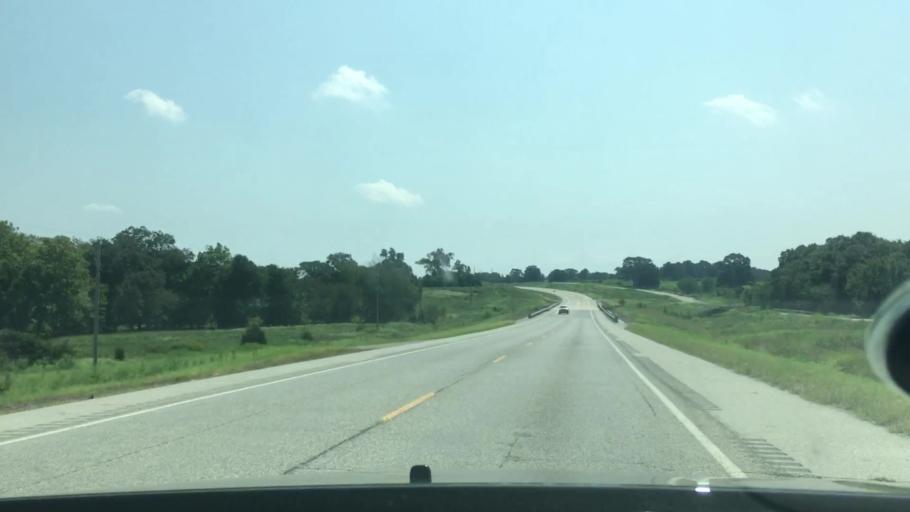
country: US
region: Oklahoma
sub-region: Atoka County
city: Atoka
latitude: 34.2924
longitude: -95.9746
